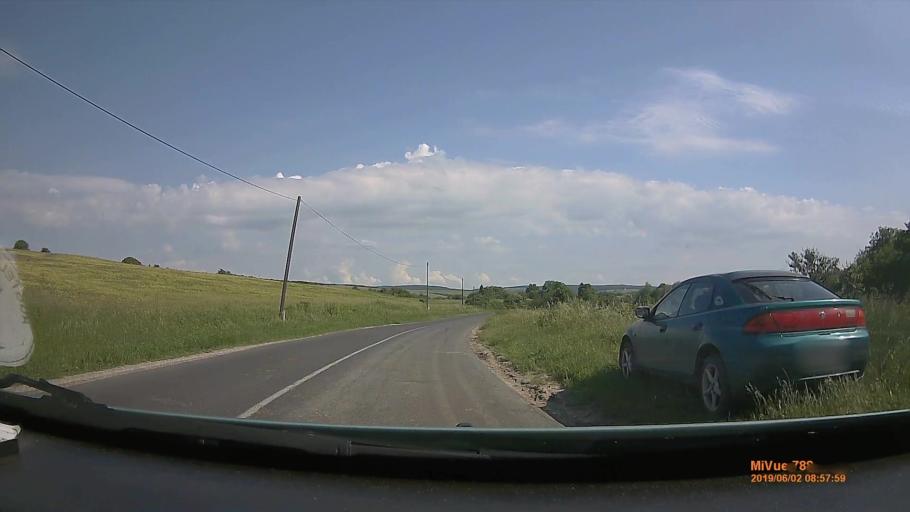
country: HU
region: Borsod-Abauj-Zemplen
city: Kazincbarcika
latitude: 48.1603
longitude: 20.6374
